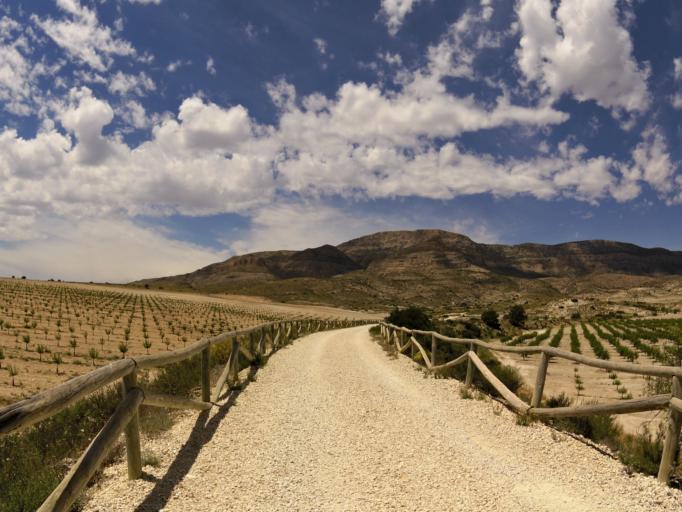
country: ES
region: Valencia
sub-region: Provincia de Alicante
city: Agost
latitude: 38.4445
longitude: -0.6836
